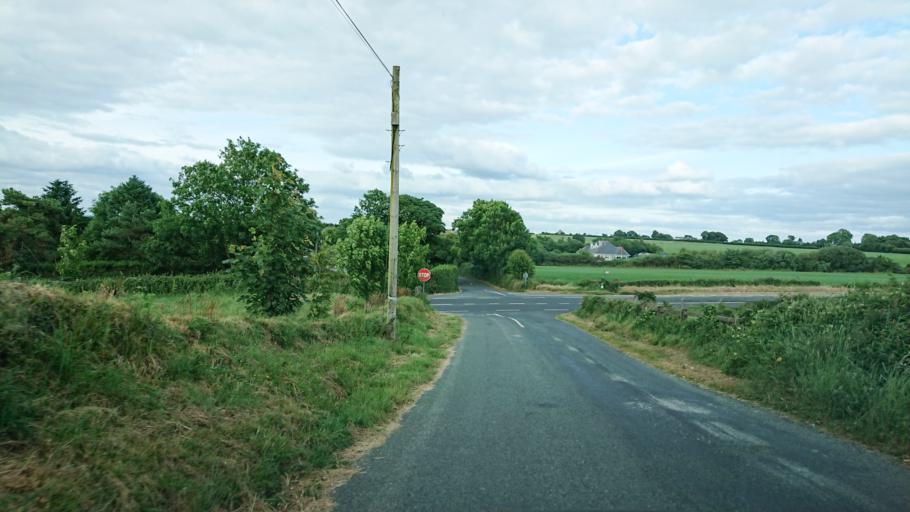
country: IE
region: Munster
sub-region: Waterford
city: Tra Mhor
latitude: 52.2134
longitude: -7.1949
